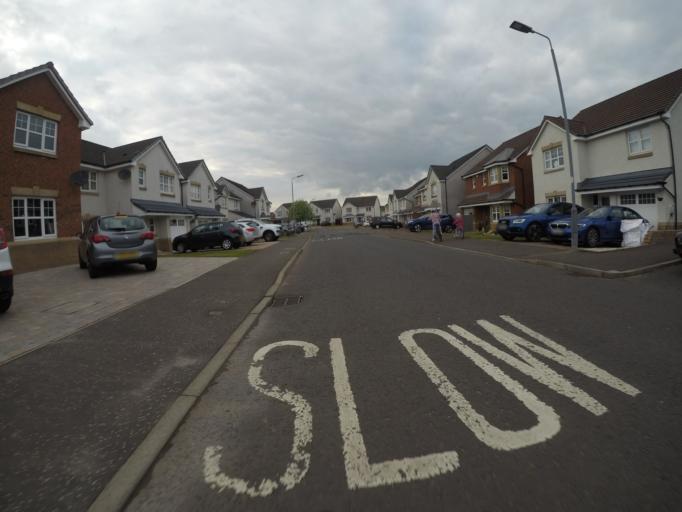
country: GB
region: Scotland
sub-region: North Ayrshire
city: Irvine
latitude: 55.6309
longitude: -4.6490
